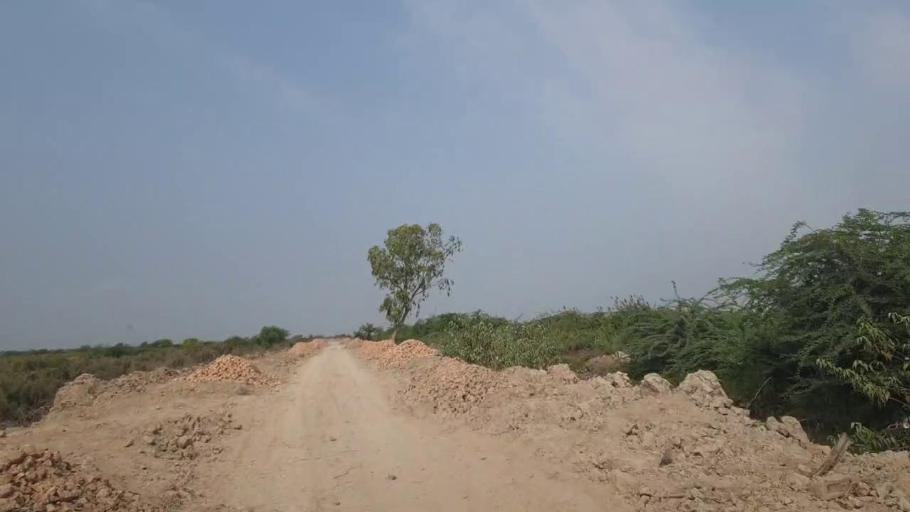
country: PK
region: Sindh
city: Badin
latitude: 24.6060
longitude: 68.7417
